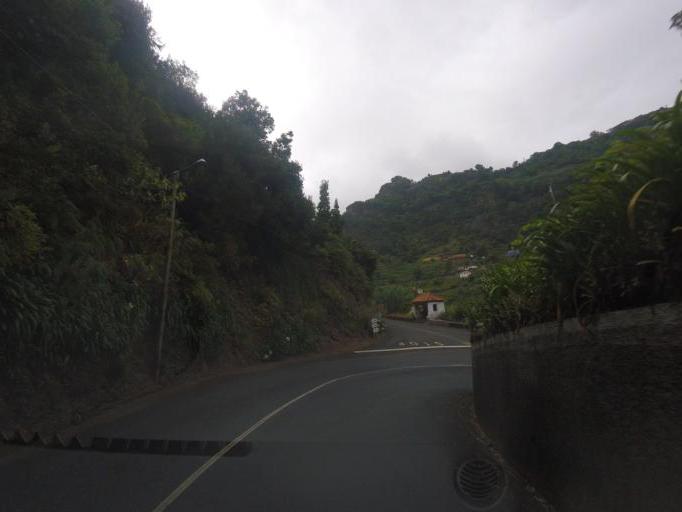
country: PT
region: Madeira
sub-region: Santana
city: Santana
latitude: 32.8149
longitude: -16.9007
